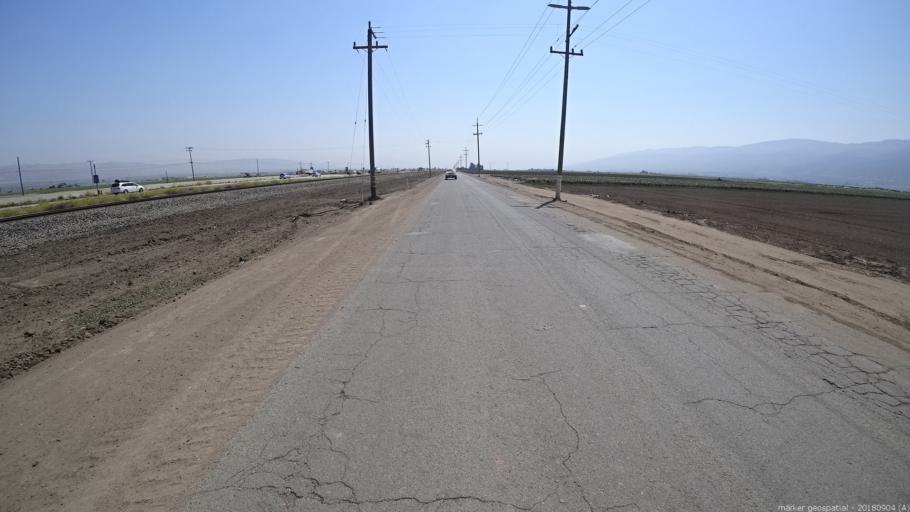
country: US
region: California
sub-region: Monterey County
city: Chualar
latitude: 36.5372
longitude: -121.4830
